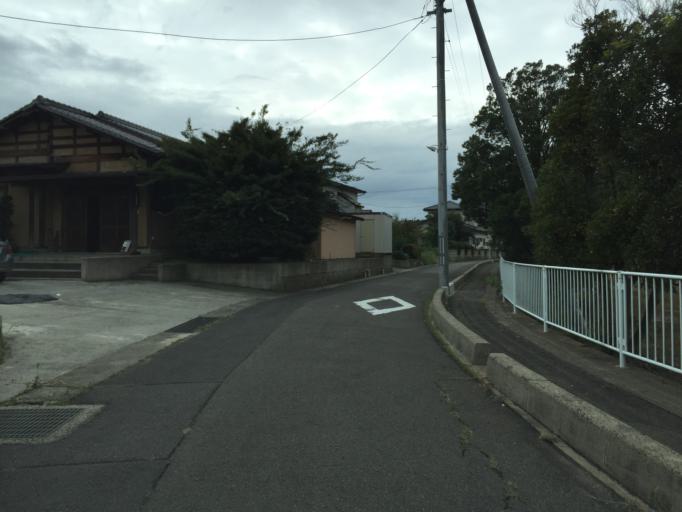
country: JP
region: Fukushima
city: Hobaramachi
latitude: 37.7908
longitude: 140.5090
